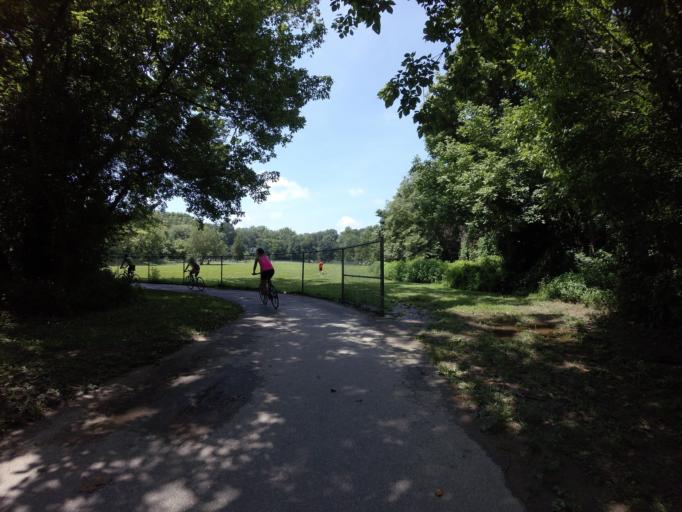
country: US
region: Maryland
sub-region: Montgomery County
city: Chevy Chase
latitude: 38.9864
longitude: -77.0583
